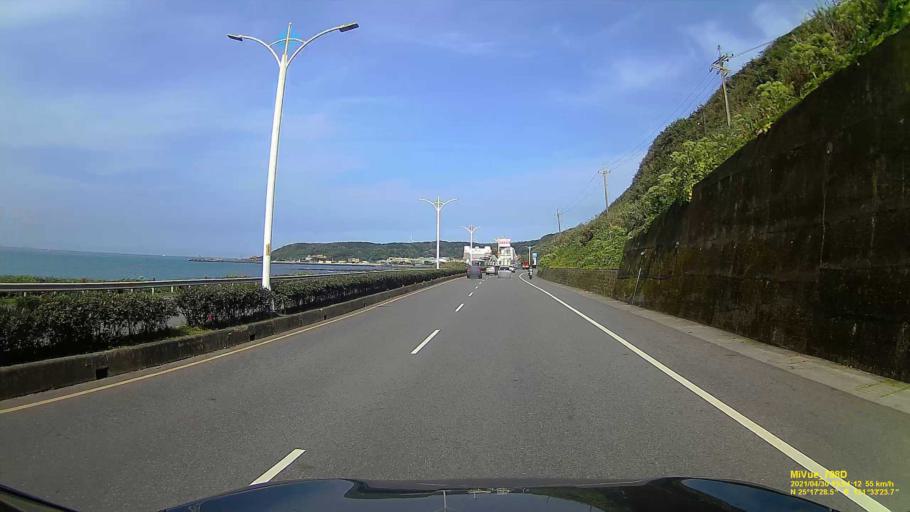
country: TW
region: Taipei
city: Taipei
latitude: 25.2912
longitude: 121.5570
